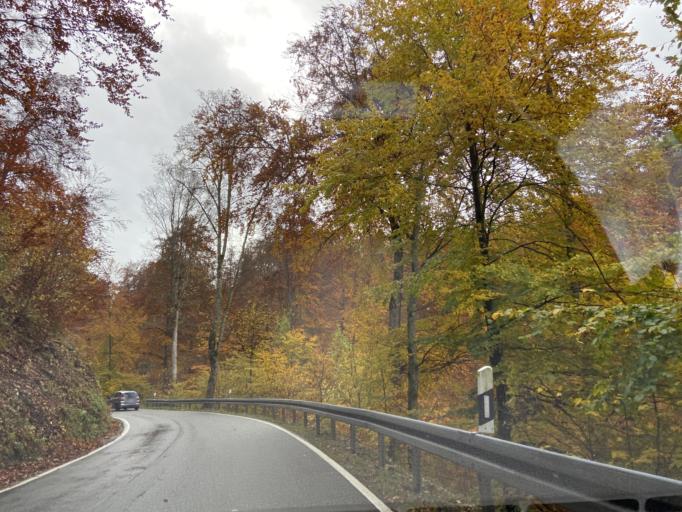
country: DE
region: Baden-Wuerttemberg
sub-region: Tuebingen Region
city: Leibertingen
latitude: 48.0684
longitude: 9.0355
